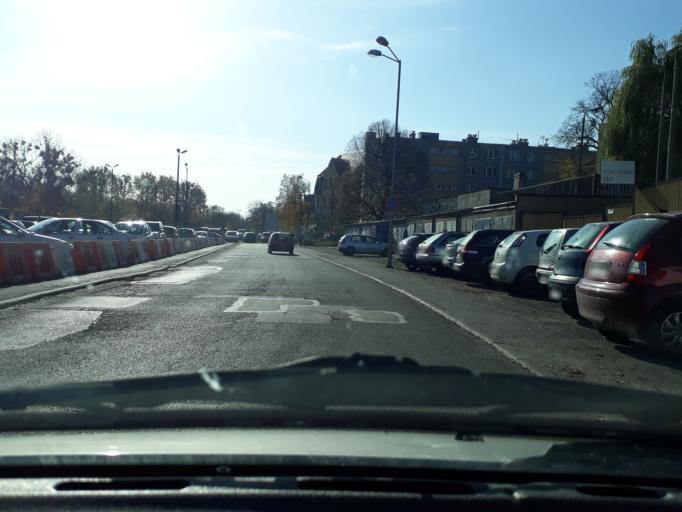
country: PL
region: Silesian Voivodeship
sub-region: Powiat tarnogorski
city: Tarnowskie Gory
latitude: 50.4439
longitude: 18.8625
